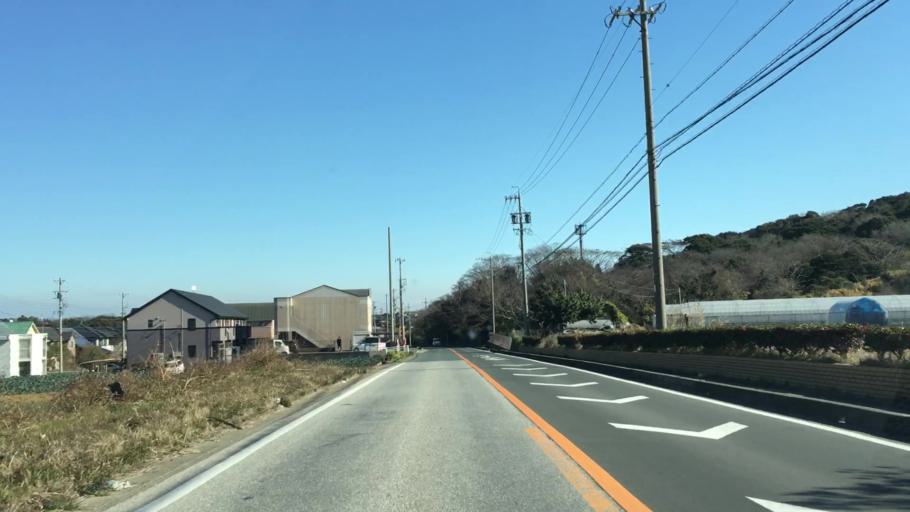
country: JP
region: Aichi
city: Tahara
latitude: 34.6925
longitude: 137.2585
